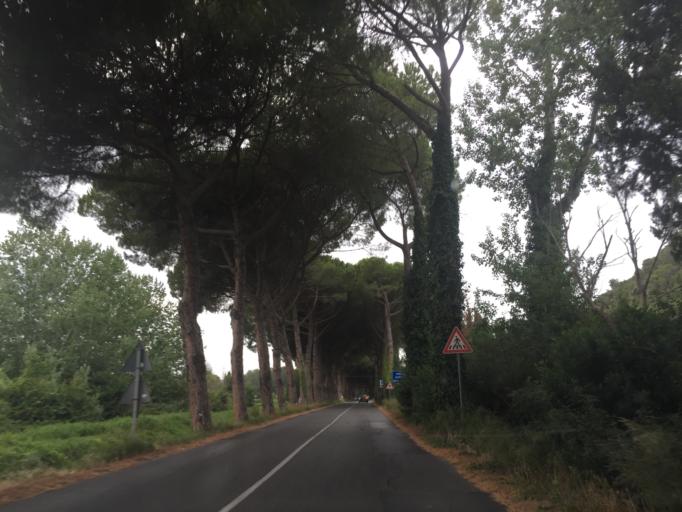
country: IT
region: Tuscany
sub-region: Province of Pisa
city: Uliveto Terme
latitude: 43.6895
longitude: 10.5329
